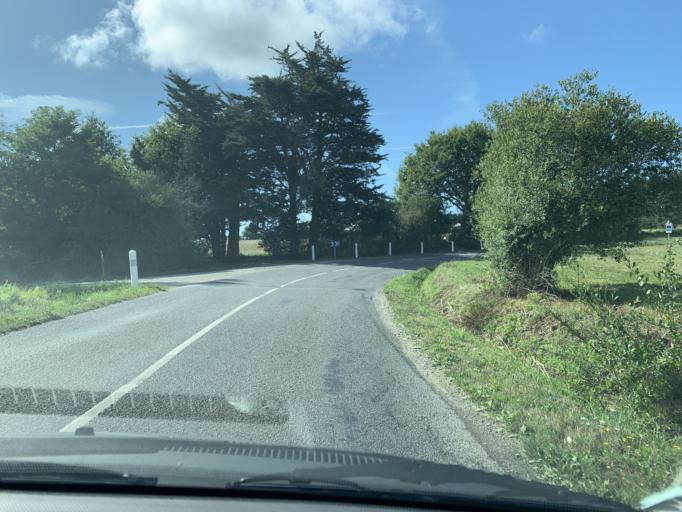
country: FR
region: Pays de la Loire
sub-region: Departement de la Loire-Atlantique
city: Asserac
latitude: 47.4338
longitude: -2.3974
